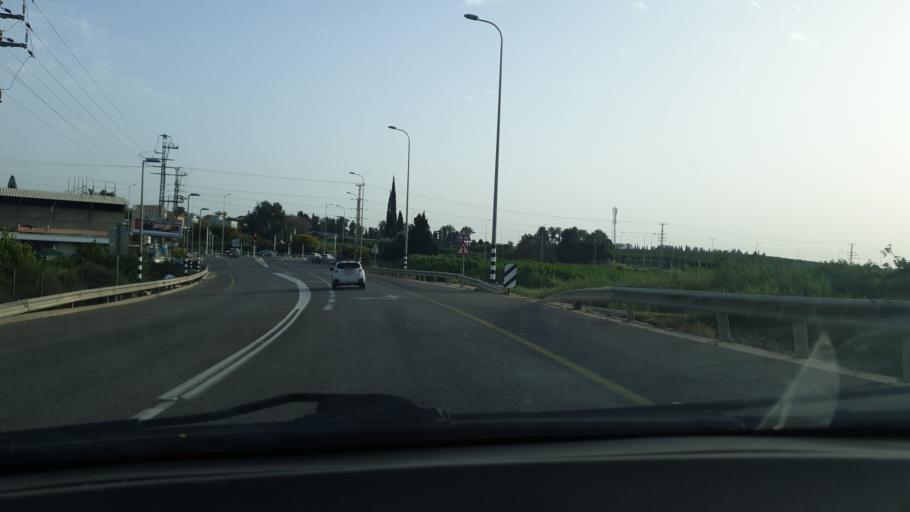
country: IL
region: Central District
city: Tel Mond
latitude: 32.2629
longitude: 34.9158
